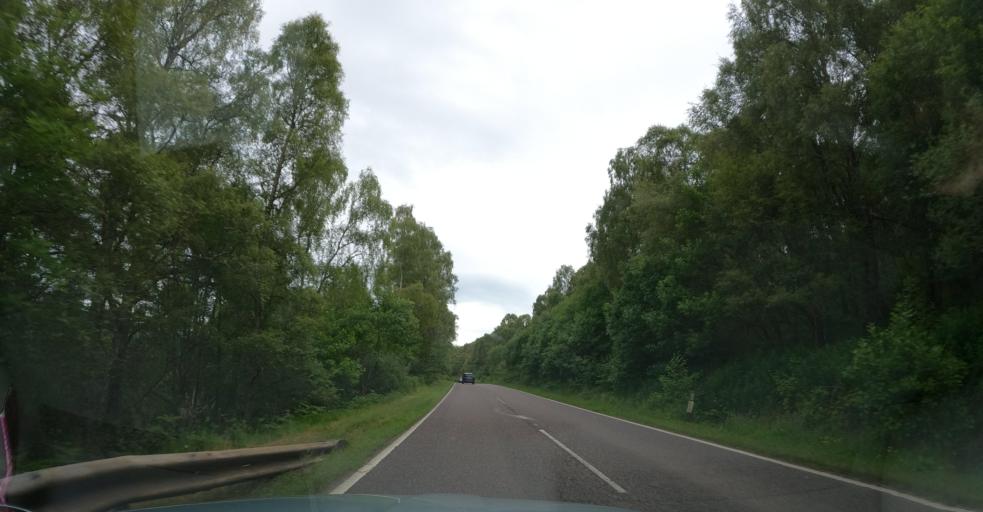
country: GB
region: Scotland
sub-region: Highland
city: Muir of Ord
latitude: 57.5927
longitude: -4.6523
